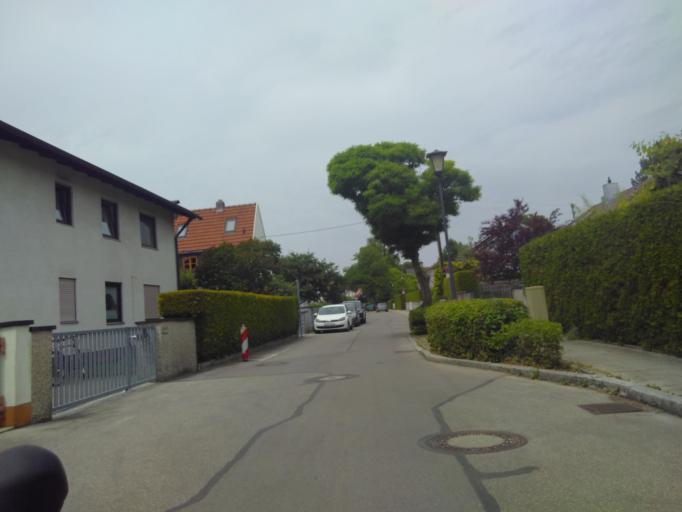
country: DE
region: Bavaria
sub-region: Upper Bavaria
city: Eichenau
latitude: 48.1624
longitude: 11.3235
